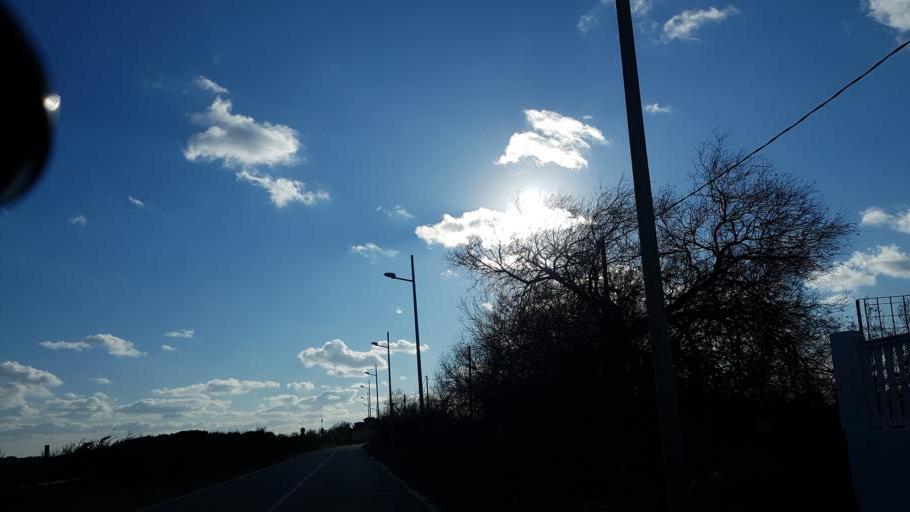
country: IT
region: Apulia
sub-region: Provincia di Brindisi
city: Materdomini
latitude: 40.6769
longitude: 17.9422
